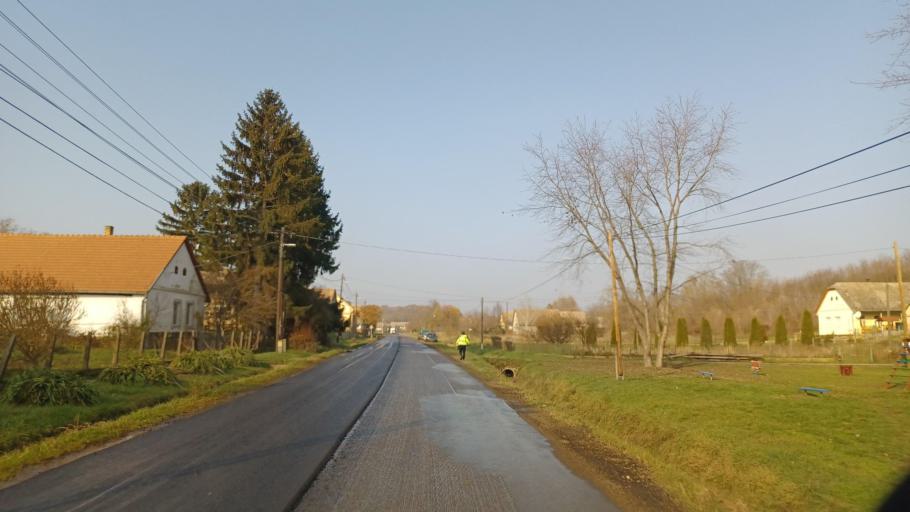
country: HU
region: Tolna
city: Zomba
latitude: 46.5021
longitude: 18.5641
